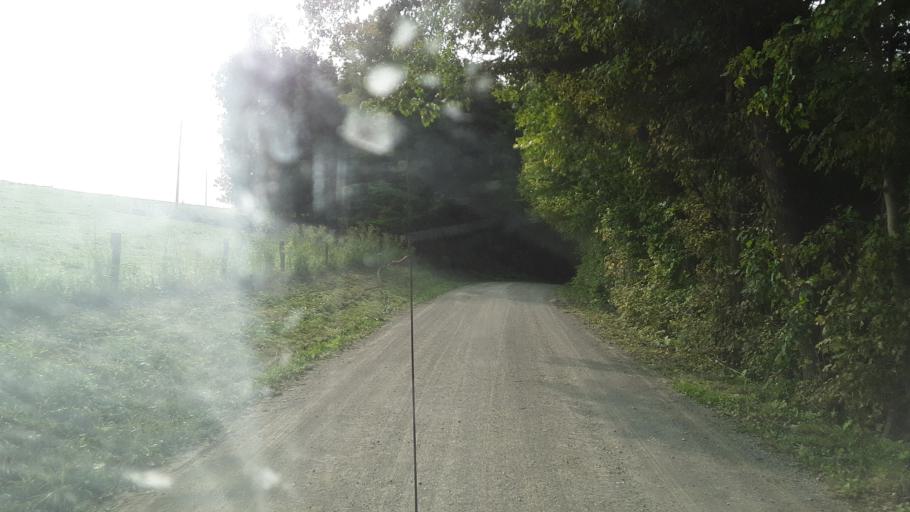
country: US
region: Ohio
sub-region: Holmes County
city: Millersburg
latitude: 40.4301
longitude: -81.8251
